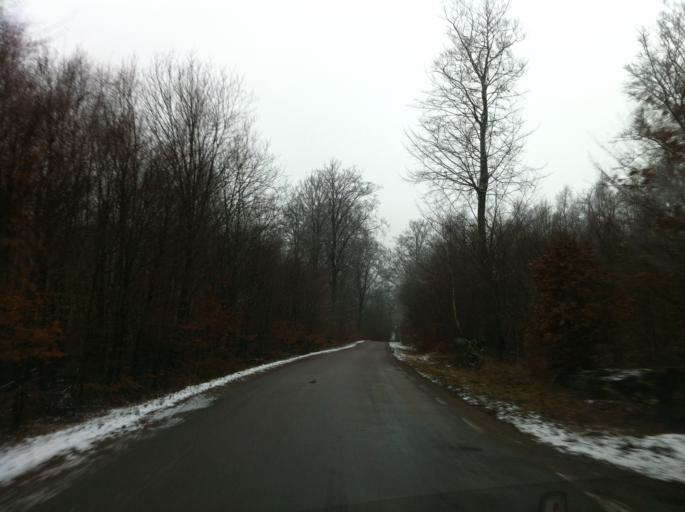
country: SE
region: Skane
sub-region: Svalovs Kommun
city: Kagerod
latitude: 55.9704
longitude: 13.0317
